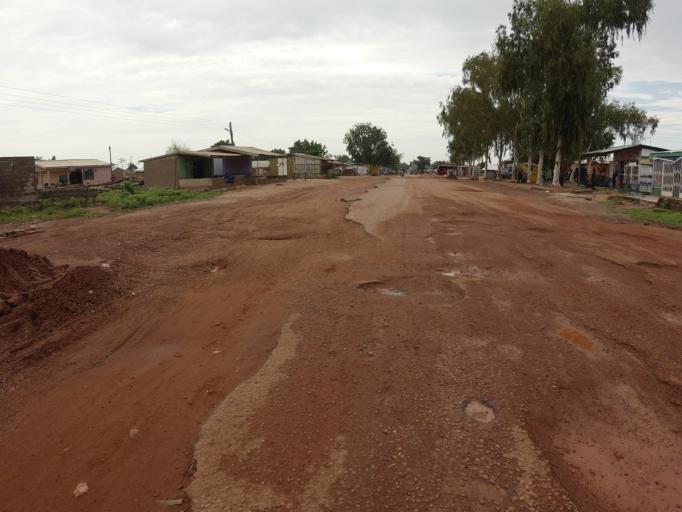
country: GH
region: Upper East
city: Bawku
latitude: 10.9372
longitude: -0.4909
